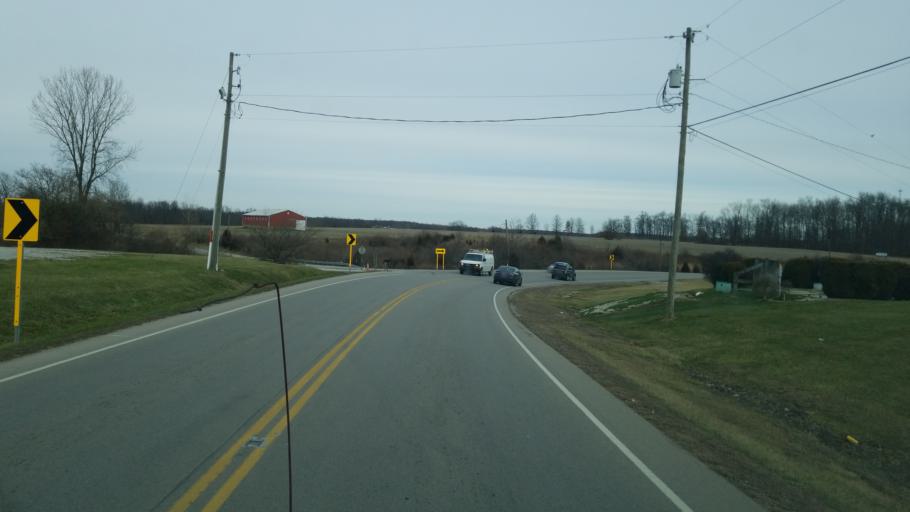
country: US
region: Ohio
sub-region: Adams County
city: Winchester
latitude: 39.0647
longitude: -83.7021
